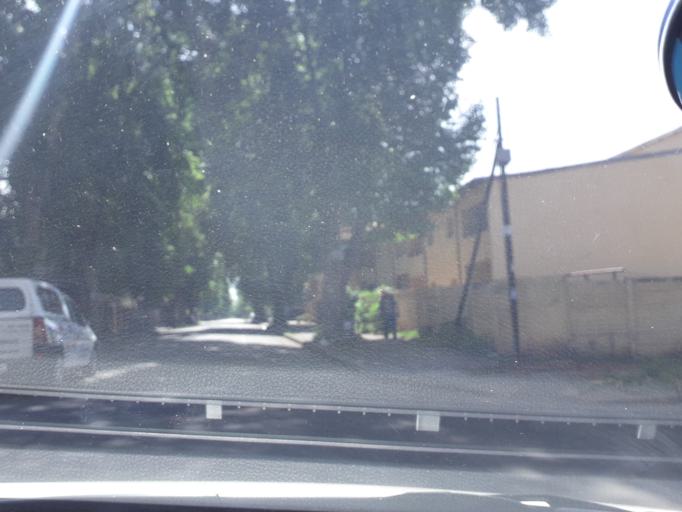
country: ZA
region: Gauteng
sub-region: City of Johannesburg Metropolitan Municipality
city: Johannesburg
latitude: -26.1910
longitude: 28.0647
